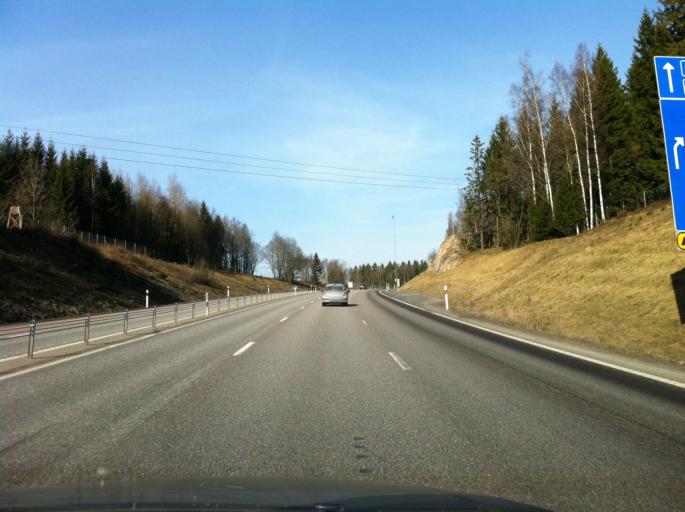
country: SE
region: Joenkoeping
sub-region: Jonkopings Kommun
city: Jonkoping
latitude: 57.7512
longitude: 14.1132
